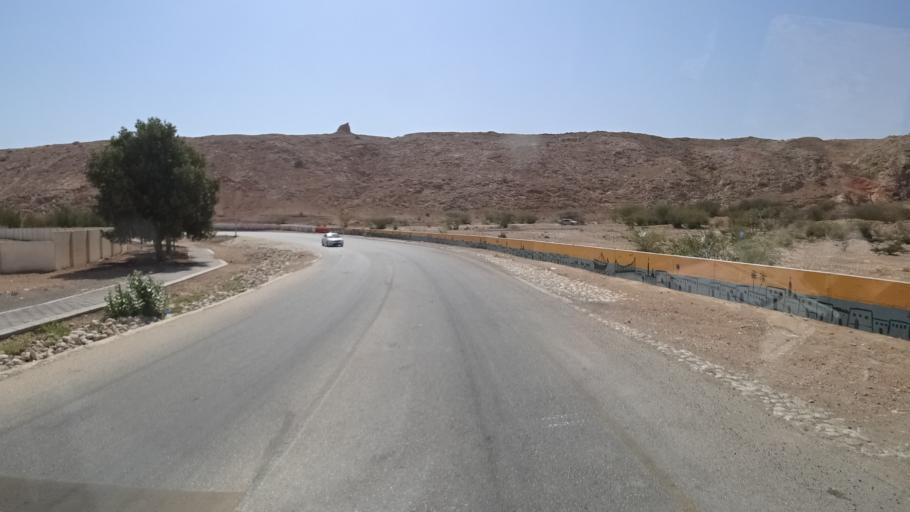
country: OM
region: Ash Sharqiyah
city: Sur
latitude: 22.5623
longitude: 59.5454
